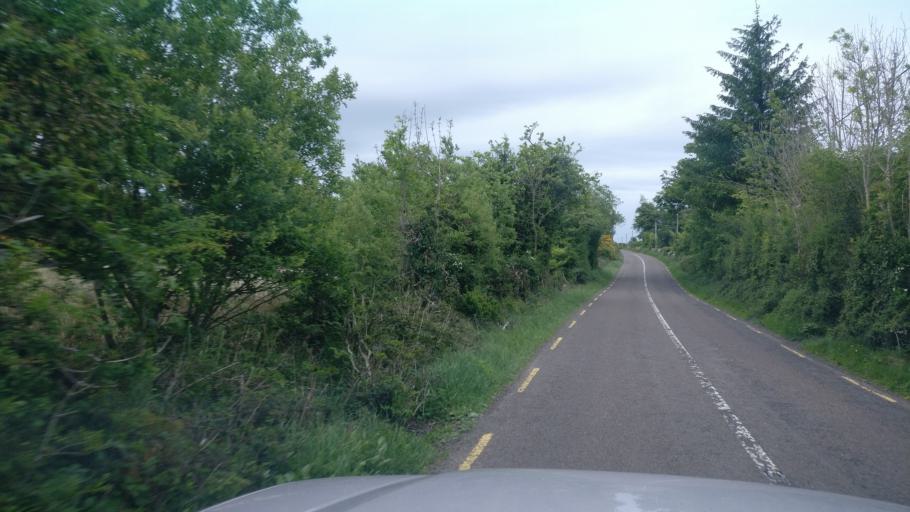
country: IE
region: Connaught
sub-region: County Galway
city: Loughrea
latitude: 53.0841
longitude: -8.5142
